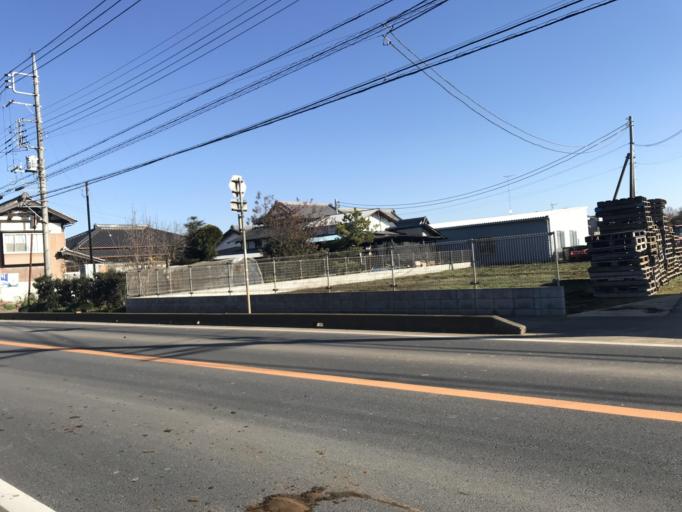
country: JP
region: Tochigi
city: Oyama
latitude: 36.2273
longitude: 139.8239
